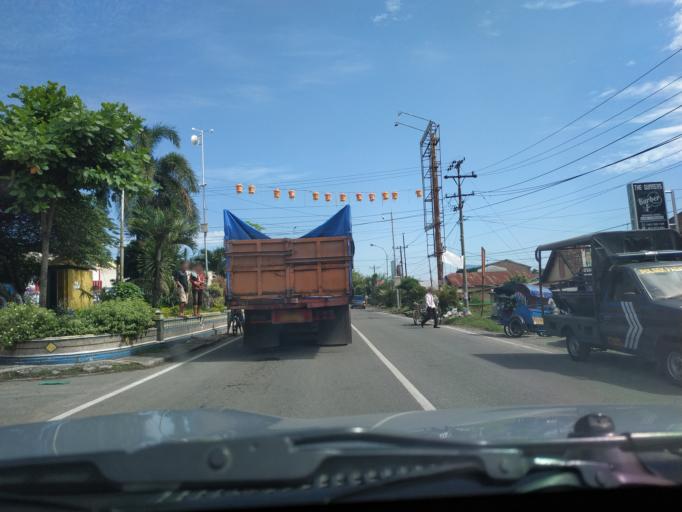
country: ID
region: North Sumatra
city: Tebingtinggi
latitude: 3.3403
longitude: 99.1729
